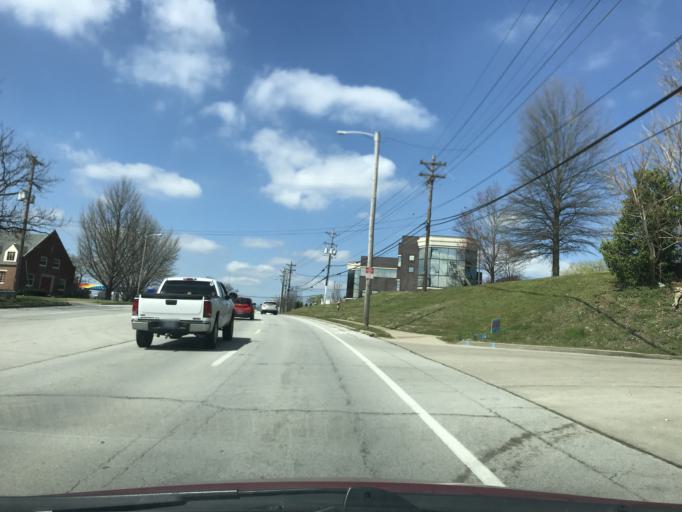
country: US
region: Kentucky
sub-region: Jefferson County
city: Audubon Park
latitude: 38.2110
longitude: -85.7182
